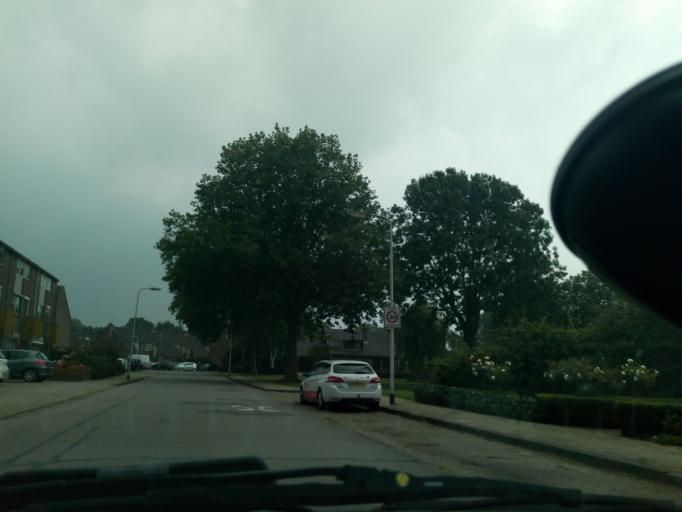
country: NL
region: South Holland
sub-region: Gemeente Alphen aan den Rijn
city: Alphen aan den Rijn
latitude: 52.1641
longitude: 4.7032
